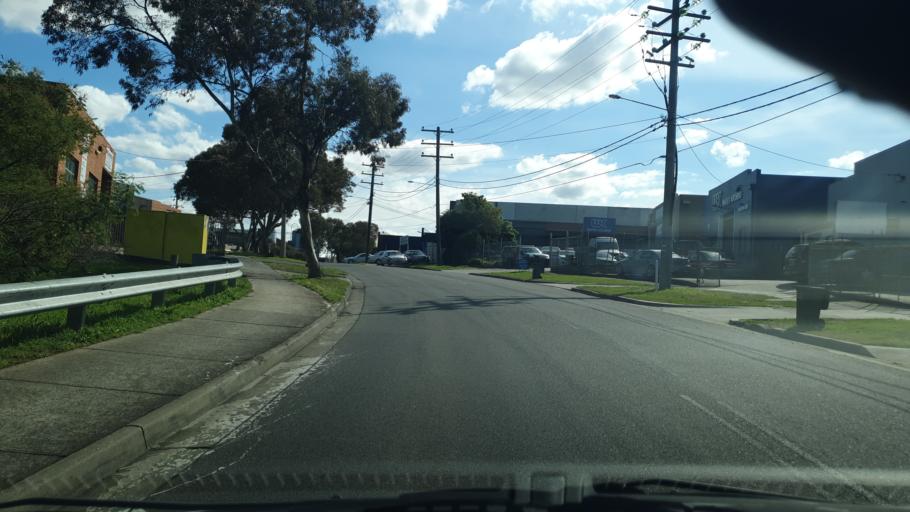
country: AU
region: Victoria
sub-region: Darebin
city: Reservoir
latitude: -37.7175
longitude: 144.9870
